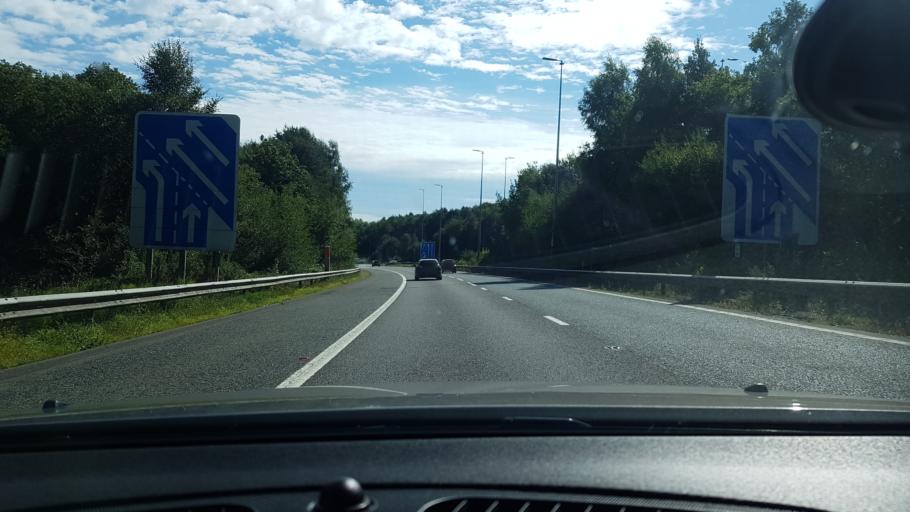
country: GB
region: England
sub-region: Southampton
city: Southampton
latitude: 50.9510
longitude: -1.3985
